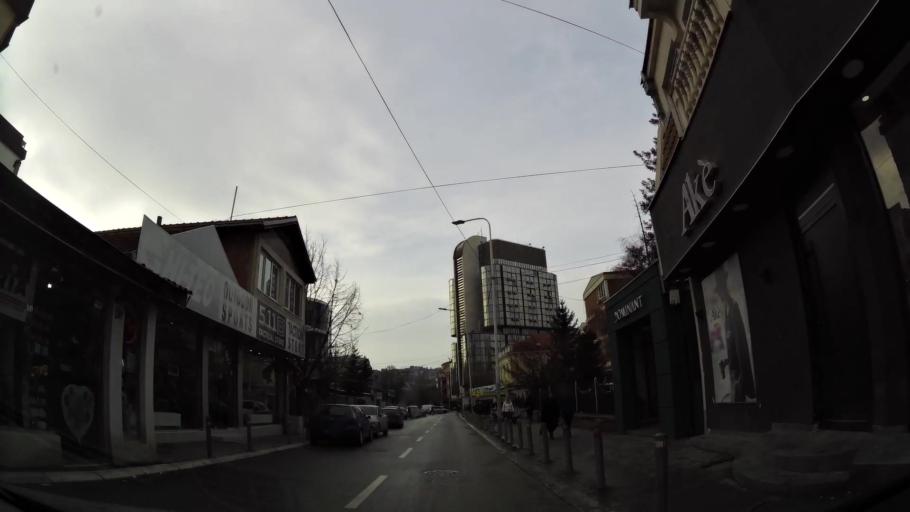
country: XK
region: Pristina
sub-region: Komuna e Prishtines
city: Pristina
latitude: 42.6634
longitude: 21.1616
